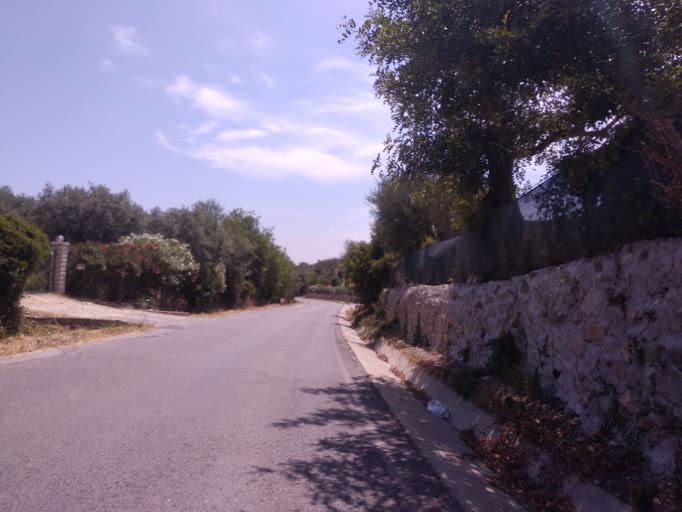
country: PT
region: Faro
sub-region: Faro
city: Santa Barbara de Nexe
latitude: 37.1165
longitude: -7.9444
